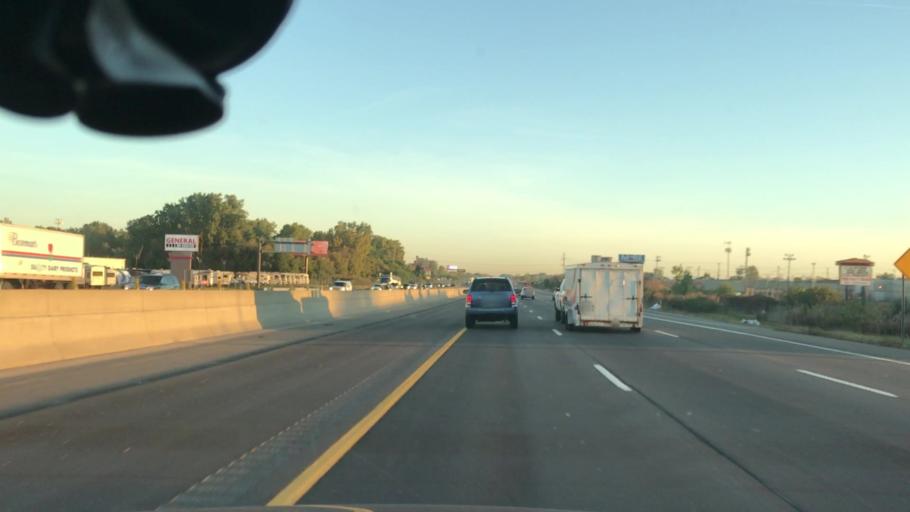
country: US
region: Michigan
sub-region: Macomb County
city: Mount Clemens
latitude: 42.5935
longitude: -82.8571
